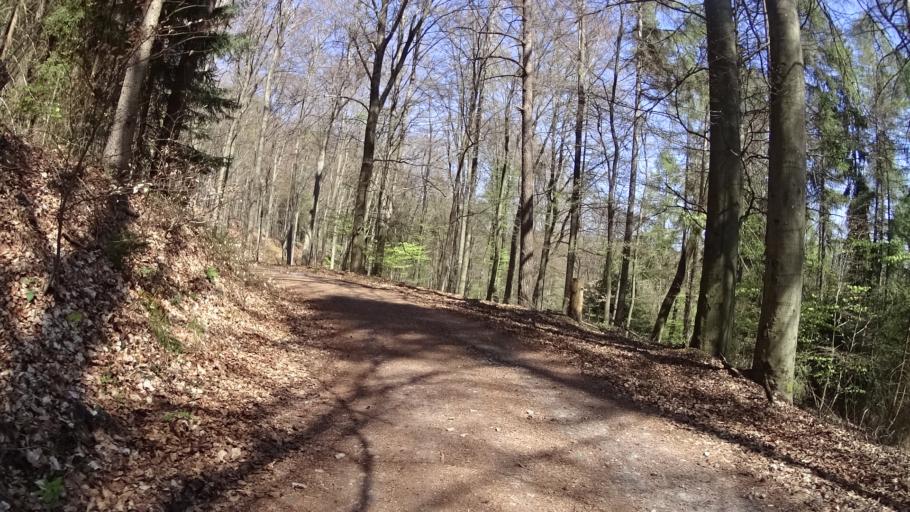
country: DE
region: Rheinland-Pfalz
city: Neidenfels
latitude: 49.4061
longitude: 8.0723
